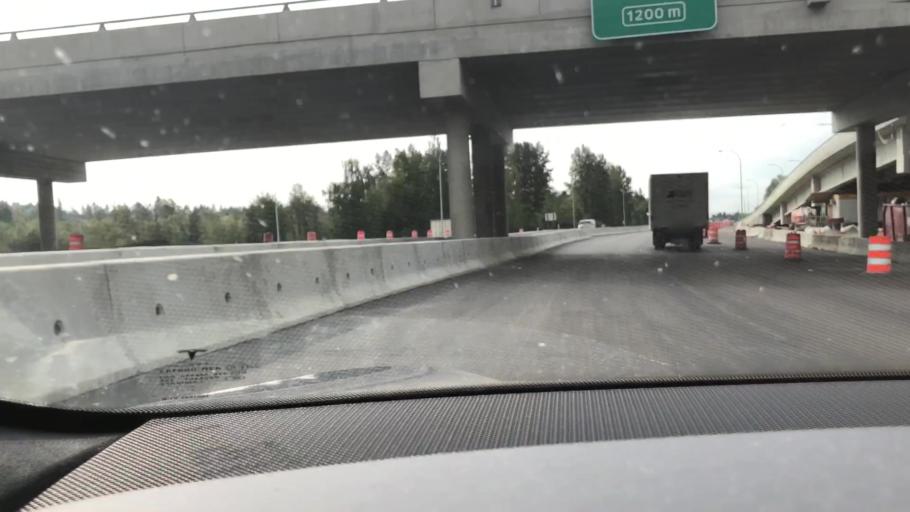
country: CA
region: British Columbia
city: Delta
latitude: 49.1338
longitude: -122.9286
